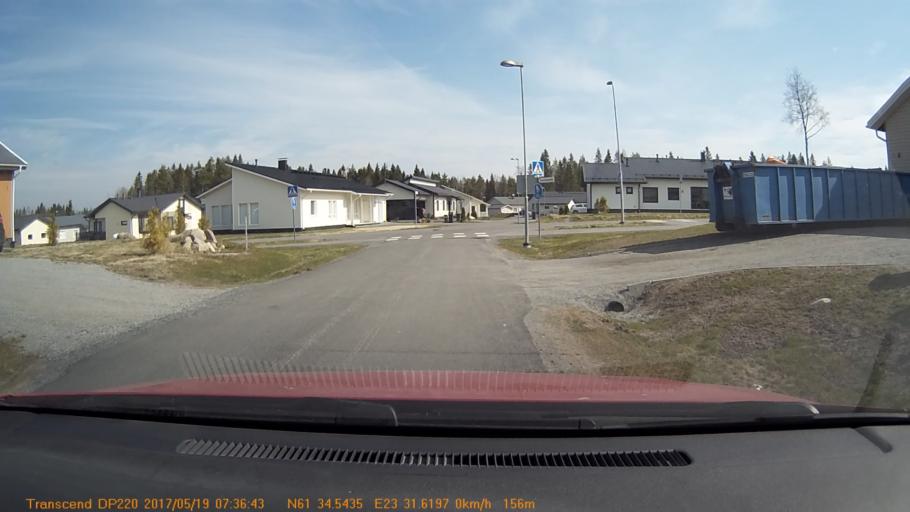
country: FI
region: Pirkanmaa
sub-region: Tampere
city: Yloejaervi
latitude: 61.5757
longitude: 23.5270
